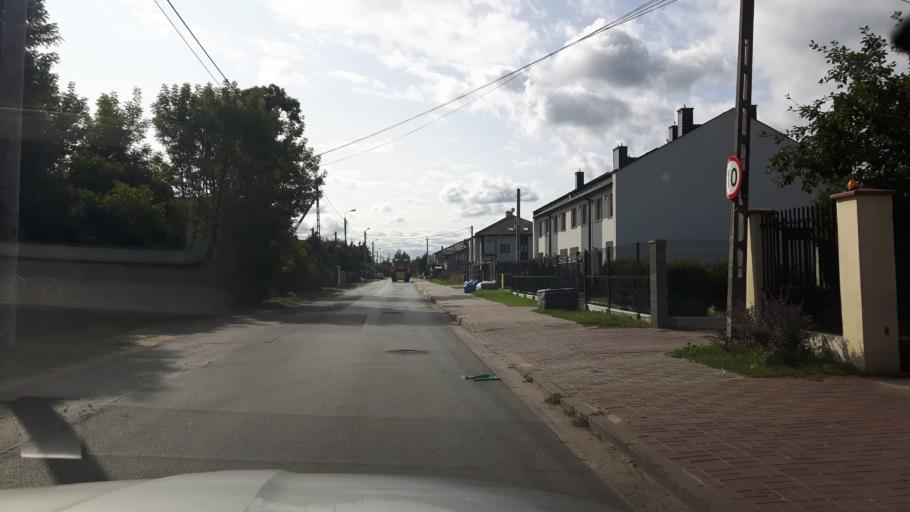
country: PL
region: Masovian Voivodeship
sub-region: Powiat wolominski
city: Marki
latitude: 52.3314
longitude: 21.0921
